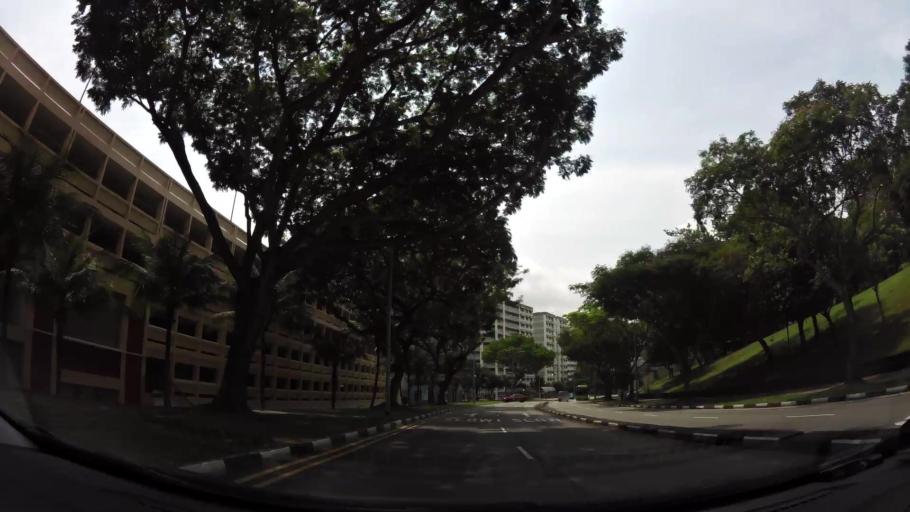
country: MY
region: Johor
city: Kampung Pasir Gudang Baru
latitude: 1.3704
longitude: 103.9607
